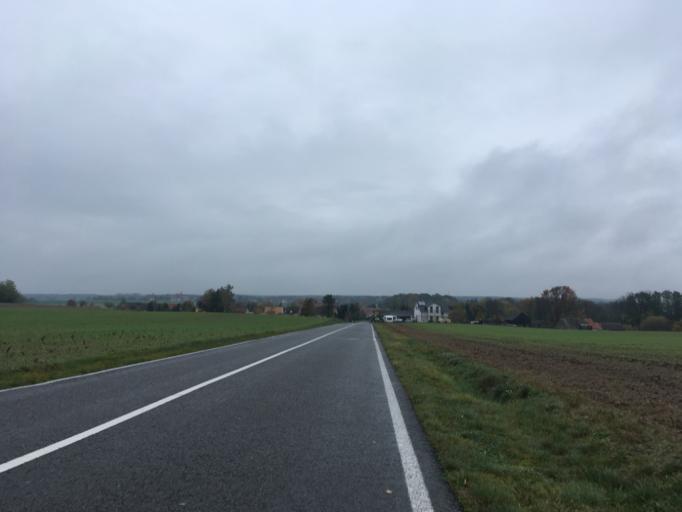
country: DE
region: Brandenburg
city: Tauche
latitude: 52.0692
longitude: 14.1845
